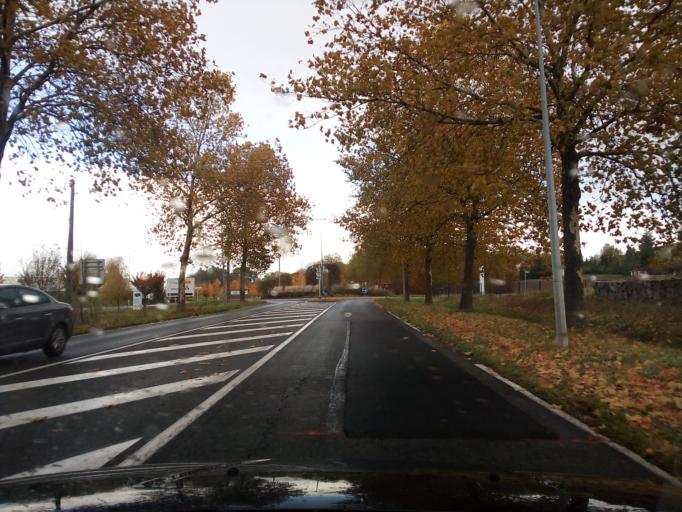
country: FR
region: Auvergne
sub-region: Departement de l'Allier
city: Saint-Pourcain-sur-Sioule
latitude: 46.3133
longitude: 3.3151
